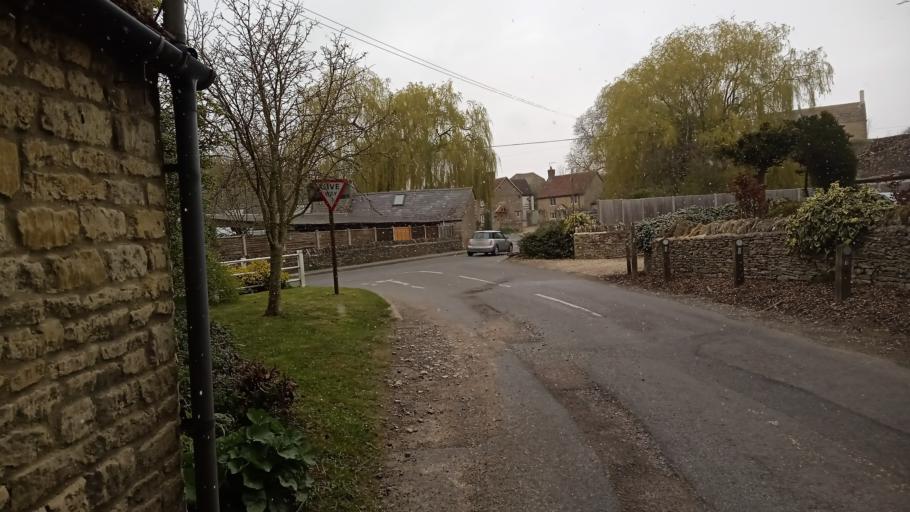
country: GB
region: England
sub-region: Oxfordshire
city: Witney
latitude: 51.8055
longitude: -1.5065
